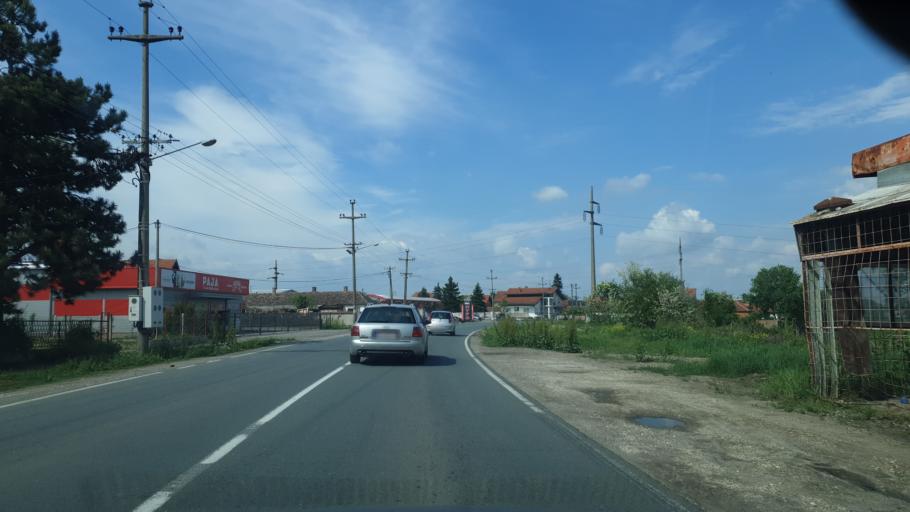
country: RS
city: Zvecka
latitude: 44.6420
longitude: 20.1834
